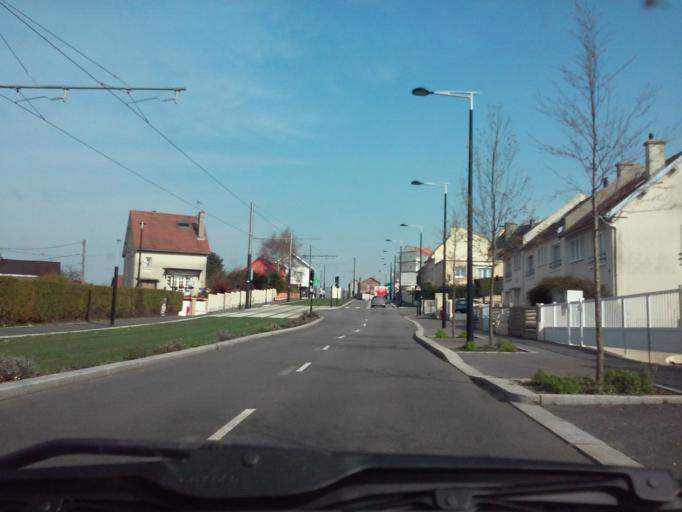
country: FR
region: Haute-Normandie
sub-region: Departement de la Seine-Maritime
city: Fontaine-la-Mallet
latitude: 49.5092
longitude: 0.1444
